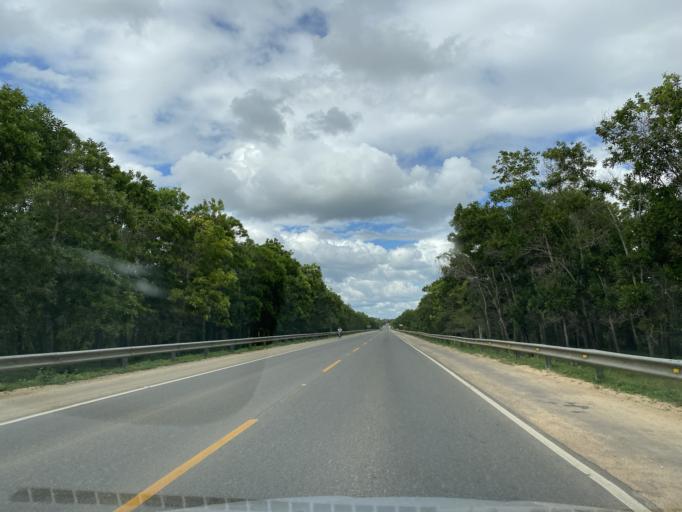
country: DO
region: Santo Domingo
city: Guerra
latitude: 18.5370
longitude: -69.7556
